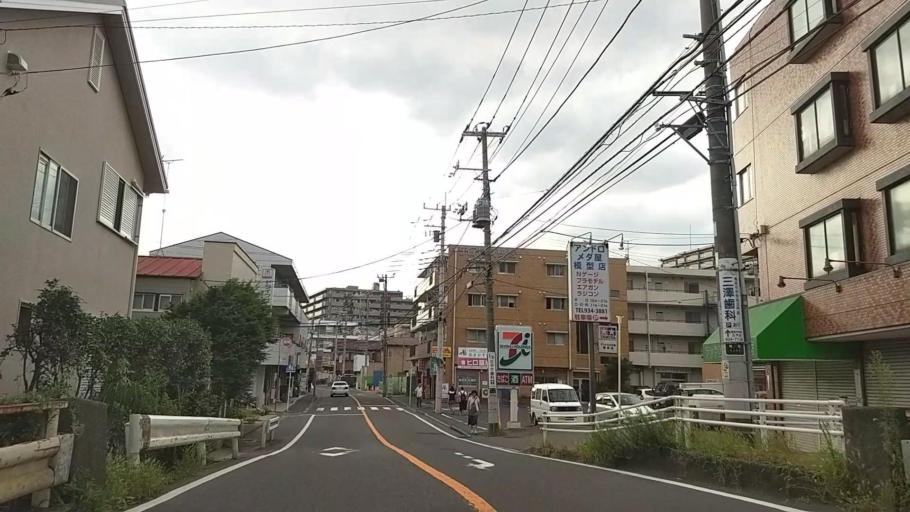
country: JP
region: Kanagawa
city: Yokohama
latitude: 35.5095
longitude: 139.5640
